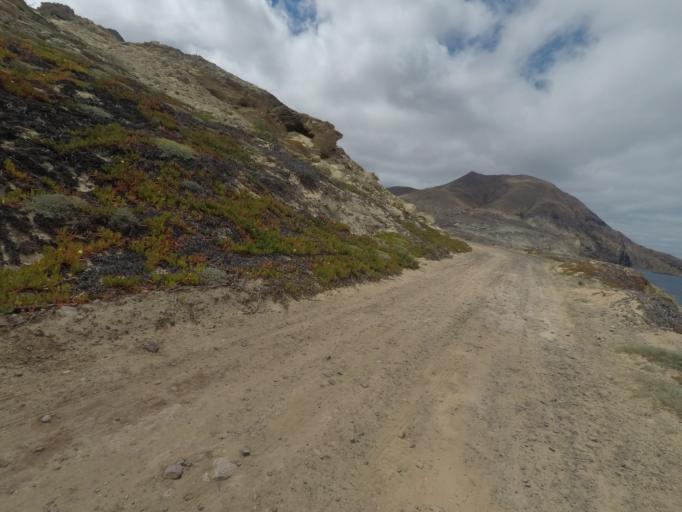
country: PT
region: Madeira
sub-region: Porto Santo
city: Vila de Porto Santo
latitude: 33.0633
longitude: -16.2954
